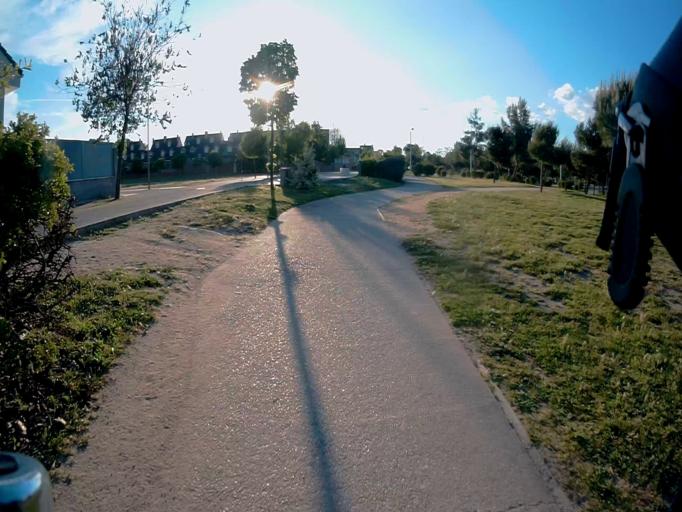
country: ES
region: Madrid
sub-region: Provincia de Madrid
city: Fuenlabrada
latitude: 40.3114
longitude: -3.7889
